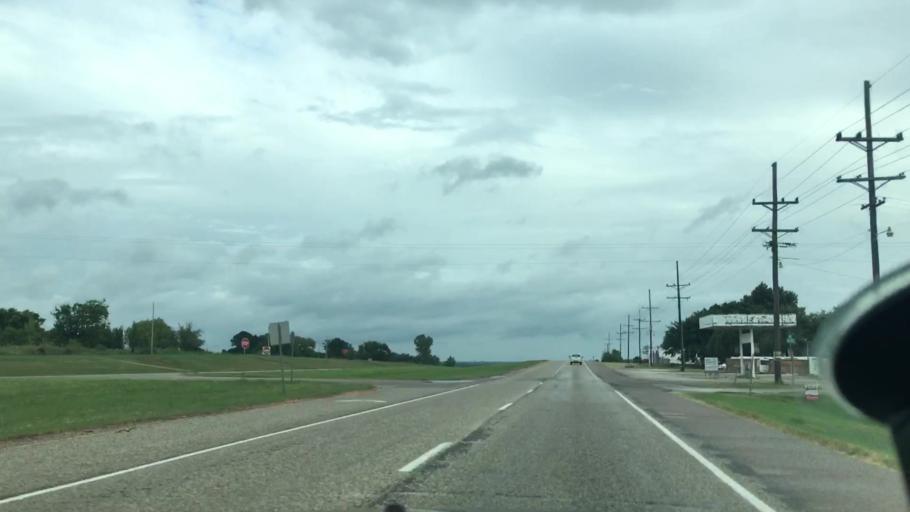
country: US
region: Oklahoma
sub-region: Seminole County
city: Seminole
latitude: 35.2906
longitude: -96.6713
